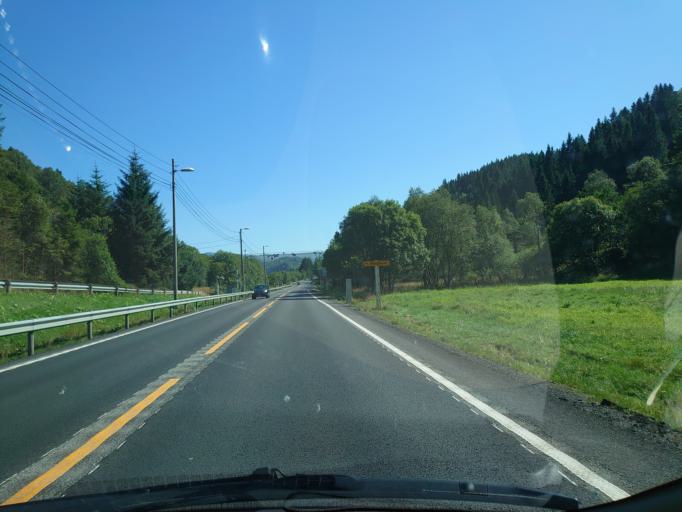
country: NO
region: Hordaland
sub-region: Bergen
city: Hylkje
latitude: 60.4700
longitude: 5.3691
